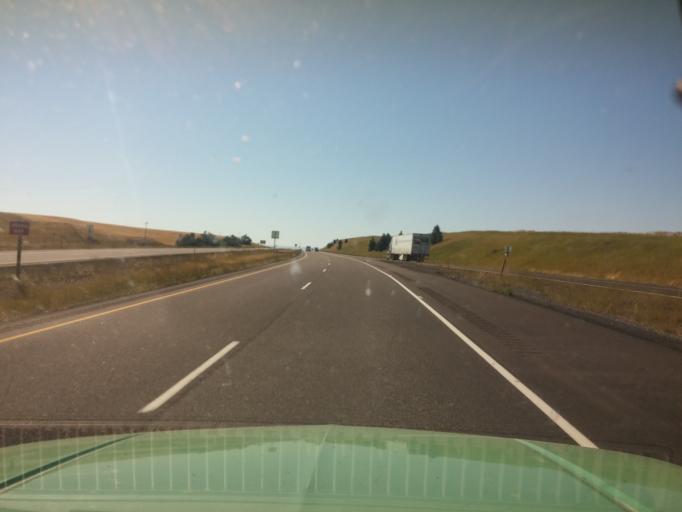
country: US
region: Washington
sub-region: Asotin County
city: Clarkston
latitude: 46.4718
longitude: -117.0347
